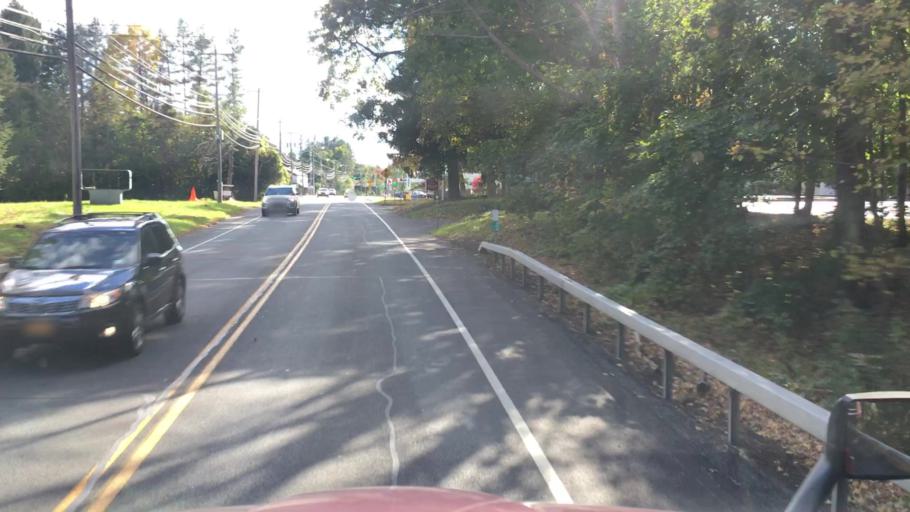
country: US
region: New York
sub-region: Schenectady County
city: East Glenville
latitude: 42.8876
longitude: -73.9246
